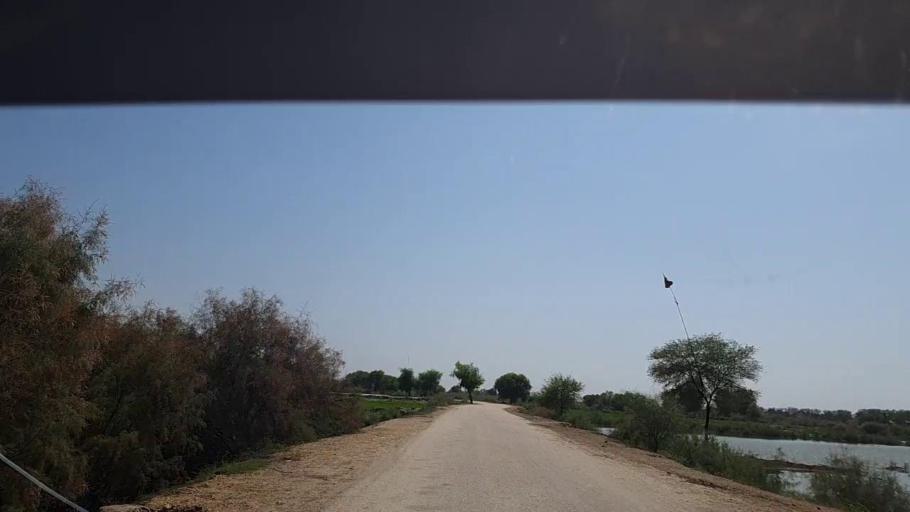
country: PK
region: Sindh
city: Ghauspur
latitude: 28.1594
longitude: 69.1603
